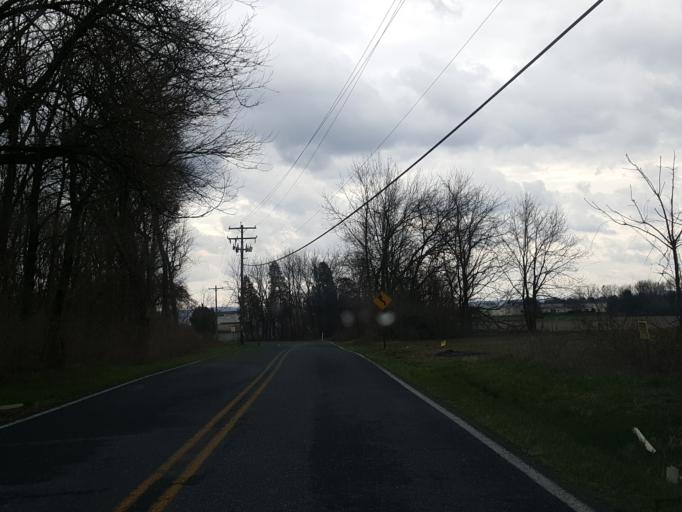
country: US
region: Pennsylvania
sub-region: Berks County
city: Fox Chase
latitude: 40.3956
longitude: -75.9867
